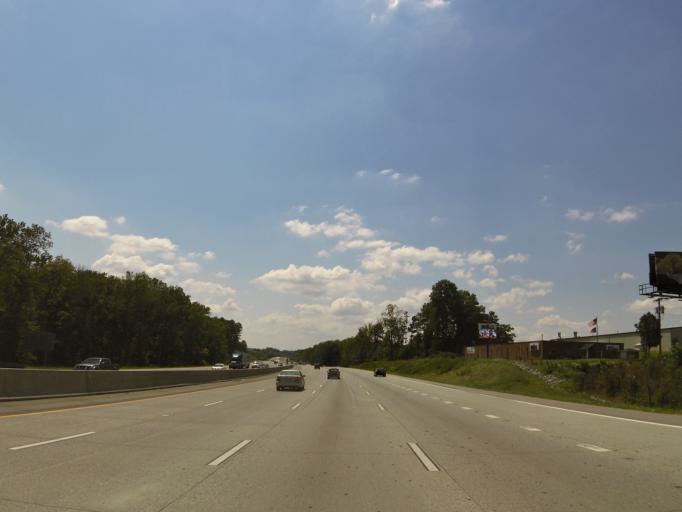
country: US
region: North Carolina
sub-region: Cabarrus County
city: Kannapolis
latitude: 35.4289
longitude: -80.6666
